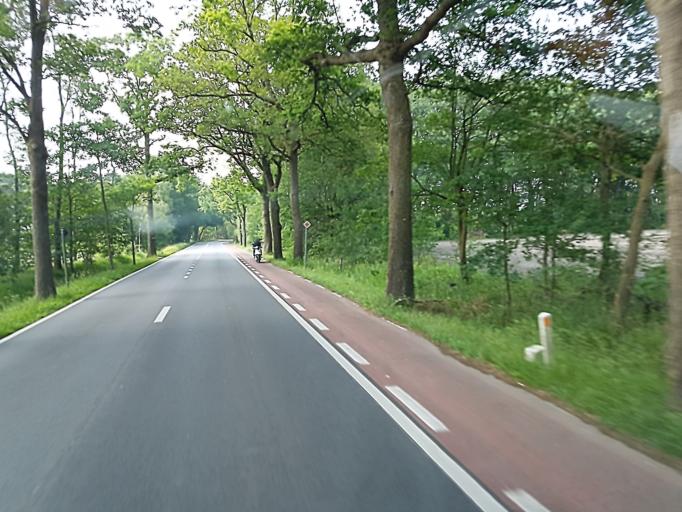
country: BE
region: Flanders
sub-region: Provincie Antwerpen
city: Turnhout
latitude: 51.3613
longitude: 4.9335
